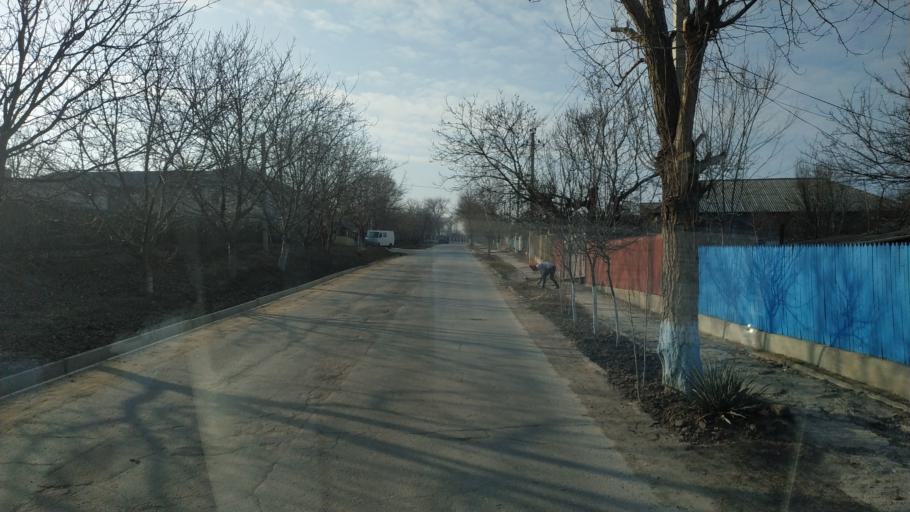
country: MD
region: Hincesti
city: Dancu
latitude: 46.7652
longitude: 28.3435
